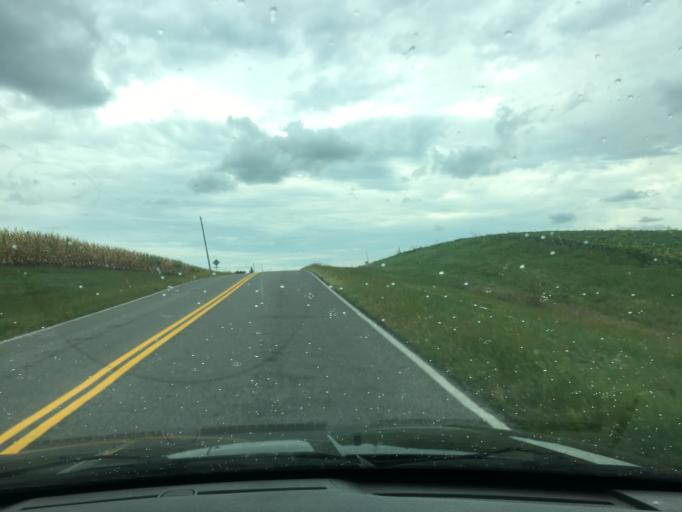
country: US
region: Ohio
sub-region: Champaign County
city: Urbana
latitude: 40.1766
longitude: -83.6904
